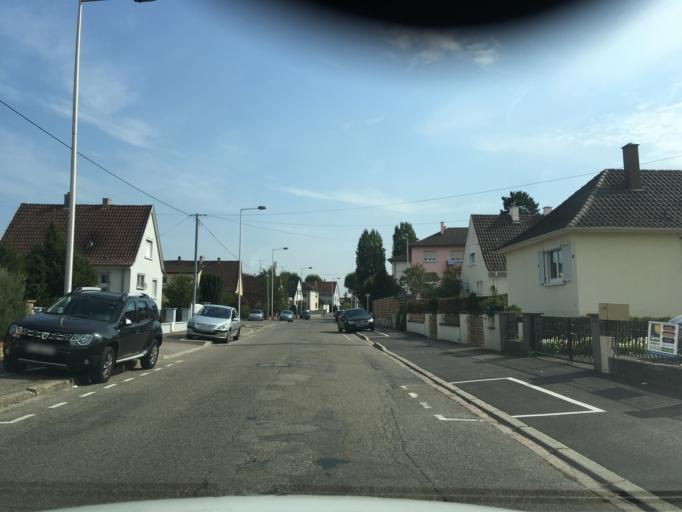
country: FR
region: Alsace
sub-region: Departement du Haut-Rhin
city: Colmar
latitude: 48.0913
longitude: 7.3675
